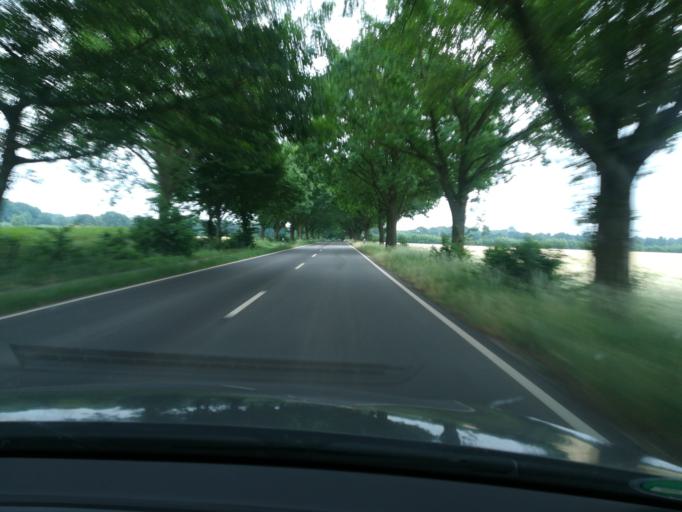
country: DE
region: Schleswig-Holstein
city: Grossensee
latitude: 53.6251
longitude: 10.3275
